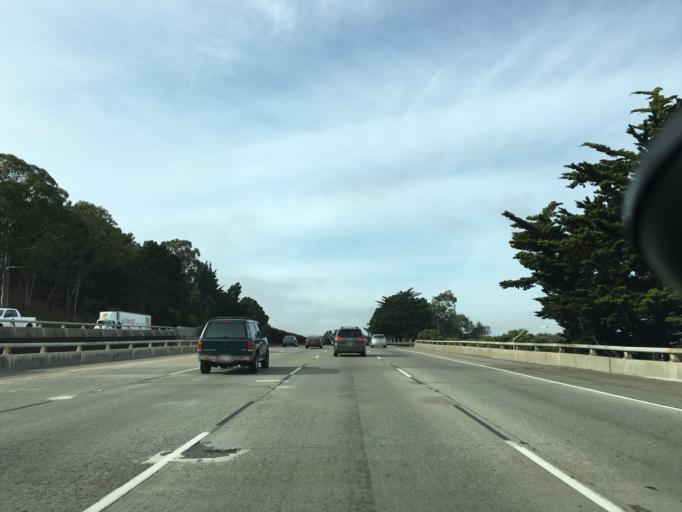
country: US
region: California
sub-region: San Mateo County
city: San Bruno
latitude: 37.6392
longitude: -122.4415
